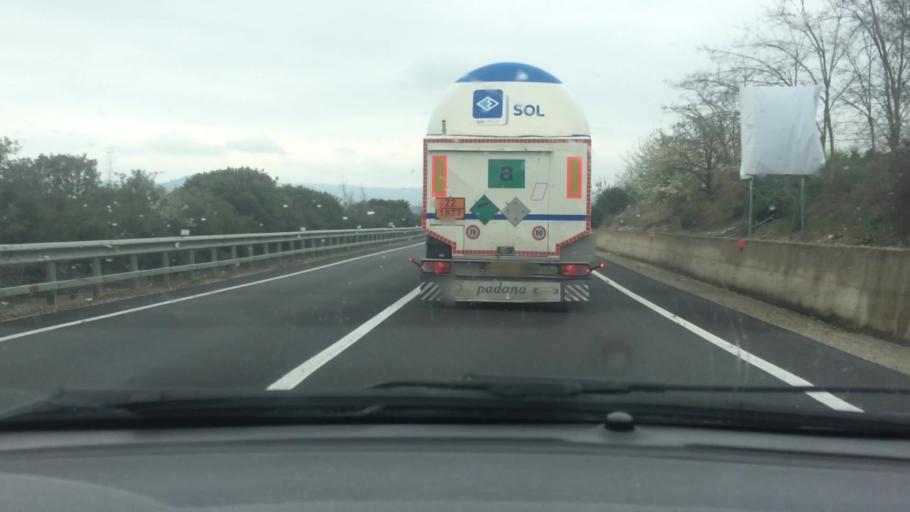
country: IT
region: Basilicate
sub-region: Provincia di Matera
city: Matera
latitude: 40.6183
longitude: 16.5820
